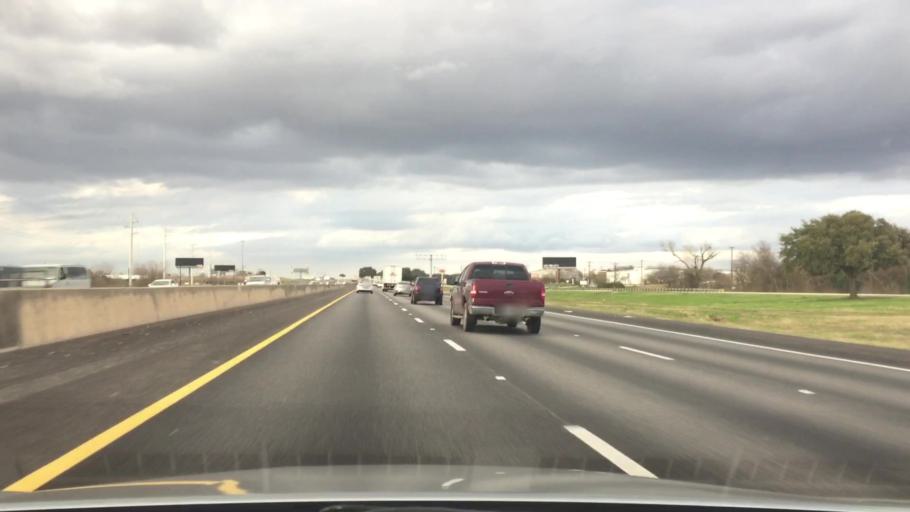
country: US
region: Texas
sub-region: Hays County
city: Kyle
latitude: 29.9637
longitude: -97.8749
